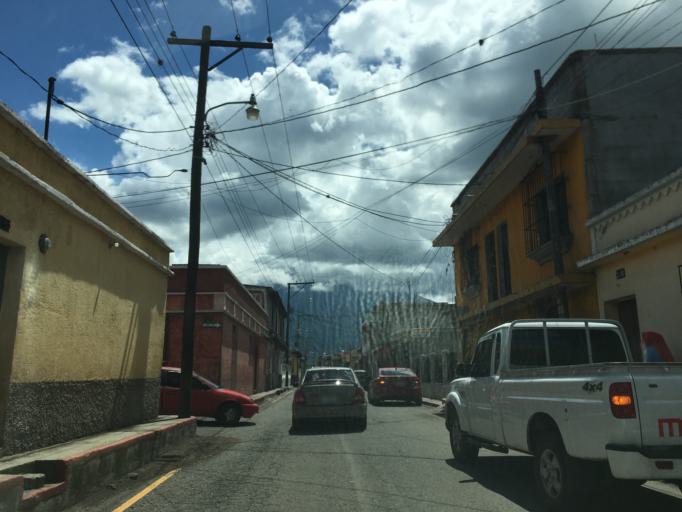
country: GT
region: Sacatepequez
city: Ciudad Vieja
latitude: 14.5260
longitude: -90.7650
